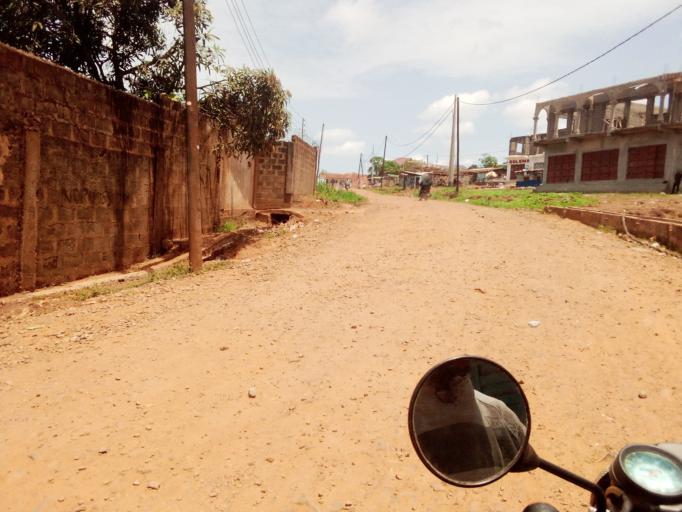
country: SL
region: Western Area
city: Waterloo
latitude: 8.3382
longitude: -13.0743
